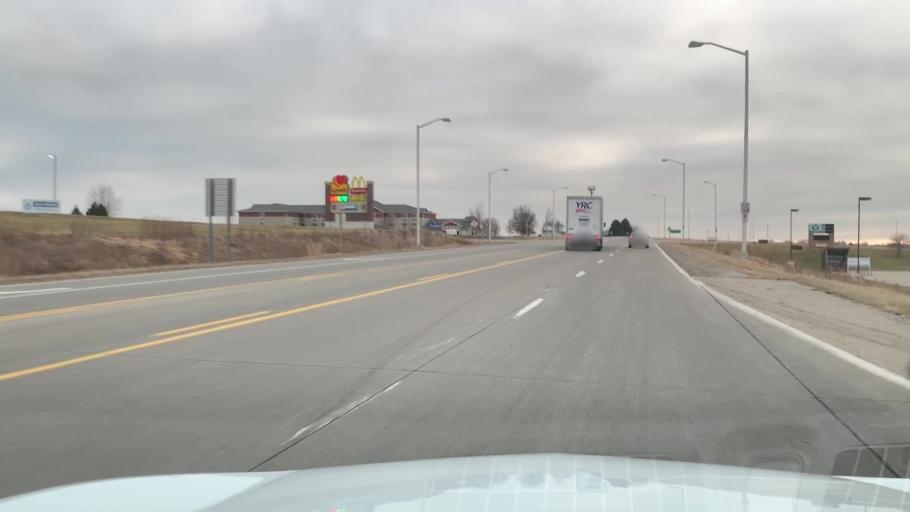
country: US
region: Iowa
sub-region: Jasper County
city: Newton
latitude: 41.6810
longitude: -92.9999
